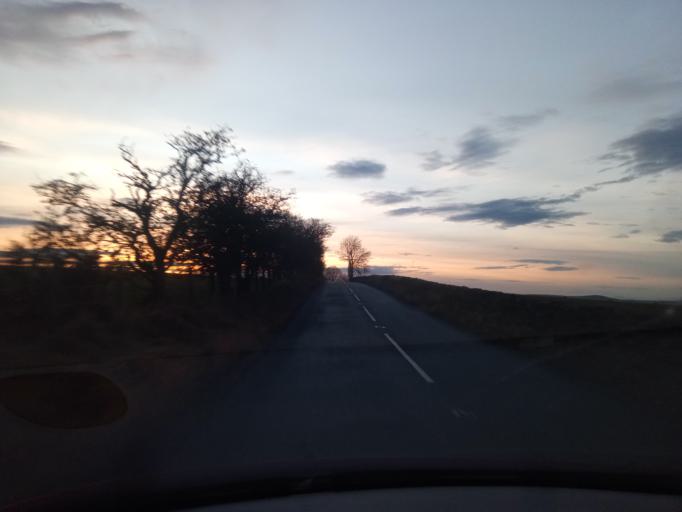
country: GB
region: England
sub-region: Northumberland
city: Otterburn
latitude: 55.2306
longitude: -2.1488
